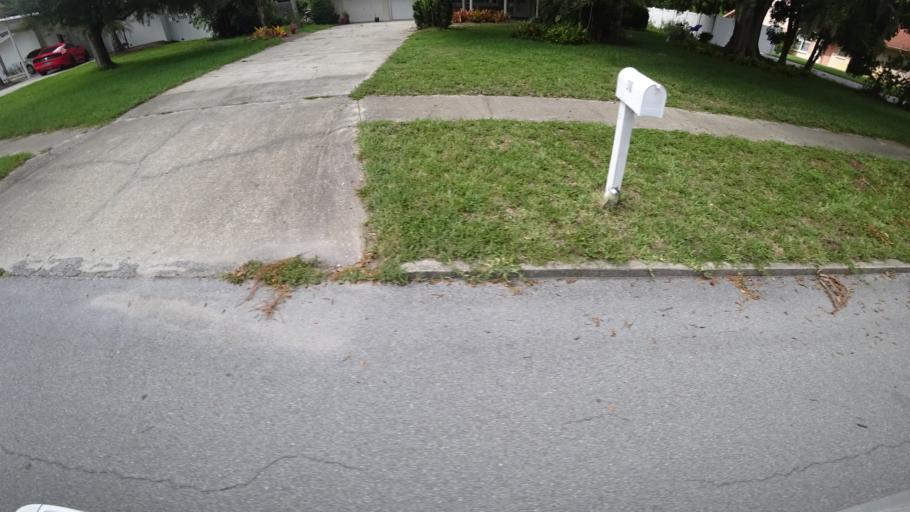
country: US
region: Florida
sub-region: Manatee County
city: Whitfield
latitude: 27.4014
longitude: -82.5693
